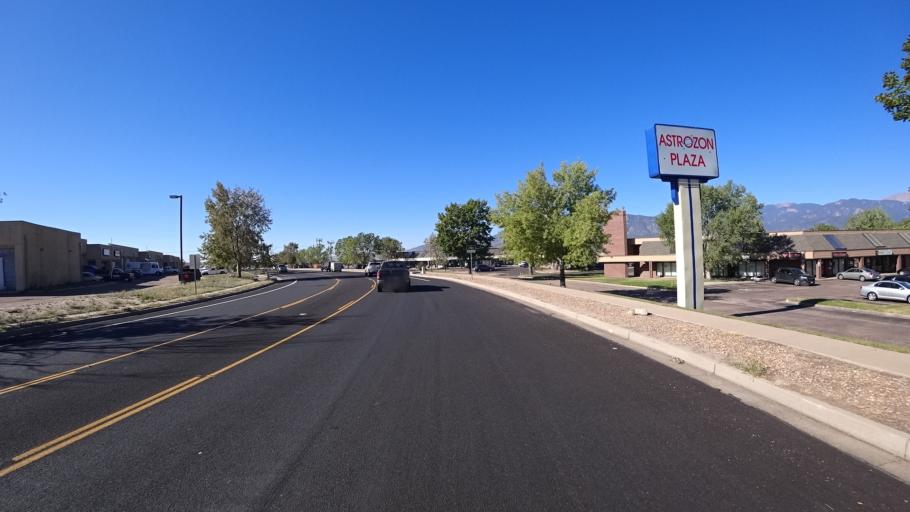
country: US
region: Colorado
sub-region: El Paso County
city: Stratmoor
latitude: 38.7961
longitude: -104.7591
